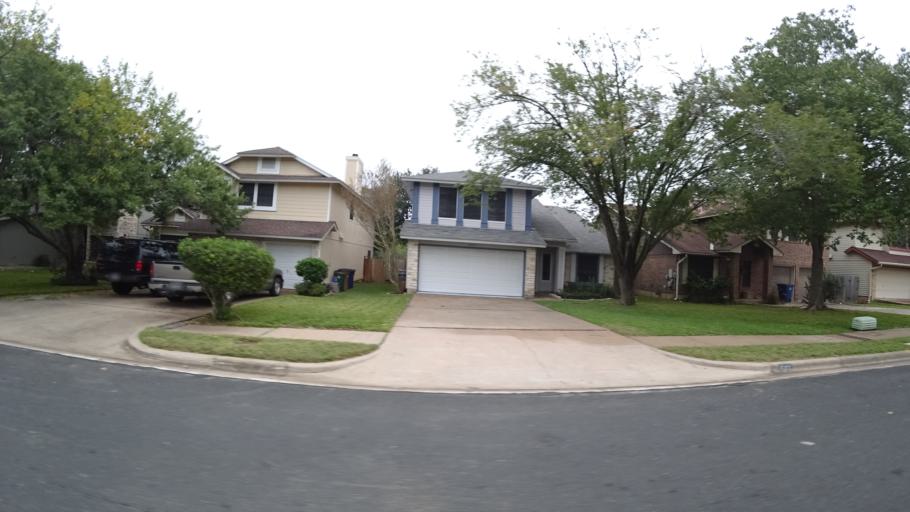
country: US
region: Texas
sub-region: Travis County
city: Shady Hollow
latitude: 30.1997
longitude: -97.8472
